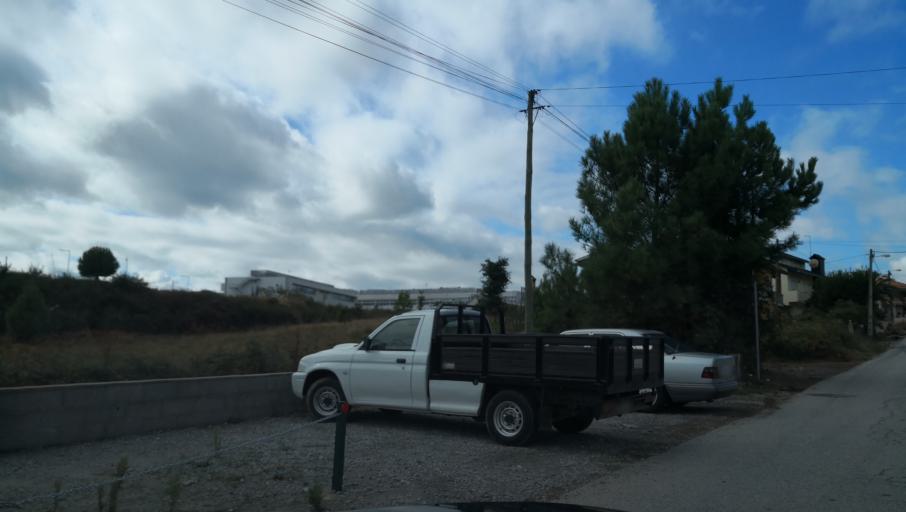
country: PT
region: Vila Real
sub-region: Vila Real
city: Vila Real
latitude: 41.2696
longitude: -7.6935
